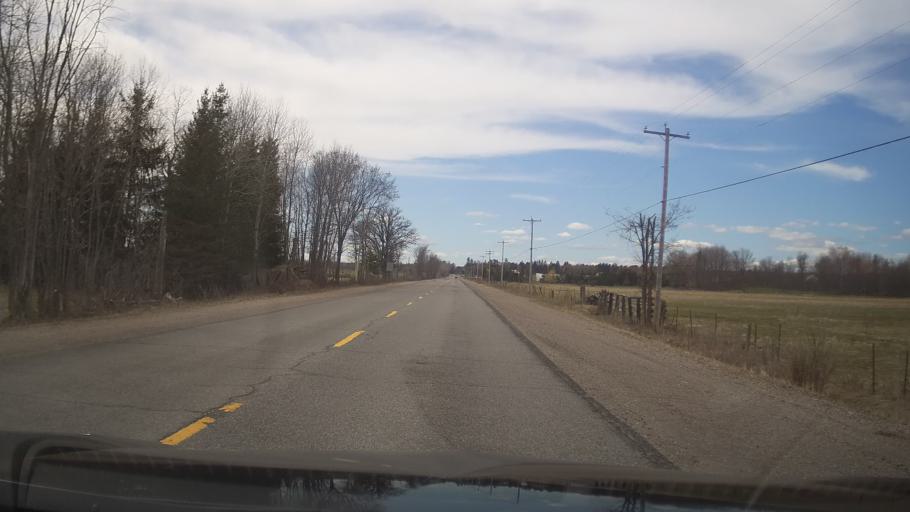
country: CA
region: Ontario
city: Arnprior
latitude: 45.5429
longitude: -76.3380
